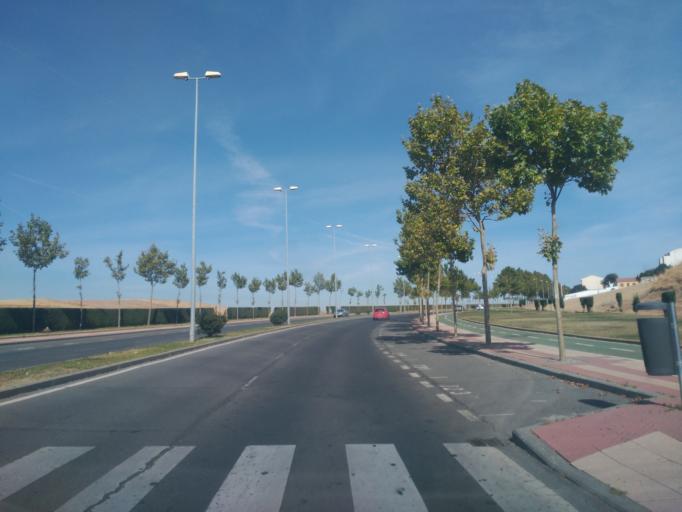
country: ES
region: Castille and Leon
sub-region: Provincia de Salamanca
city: Salamanca
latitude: 40.9780
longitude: -5.6831
